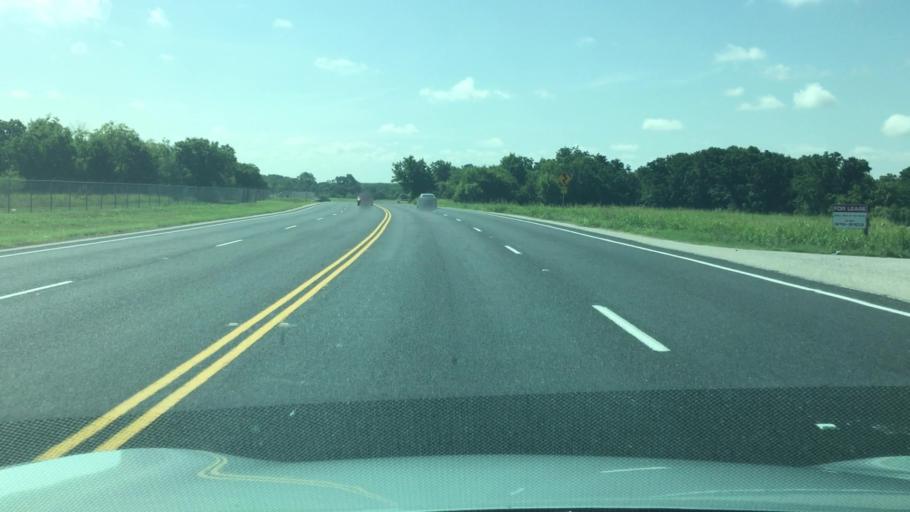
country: US
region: Texas
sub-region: Travis County
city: Austin
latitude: 30.1794
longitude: -97.6838
